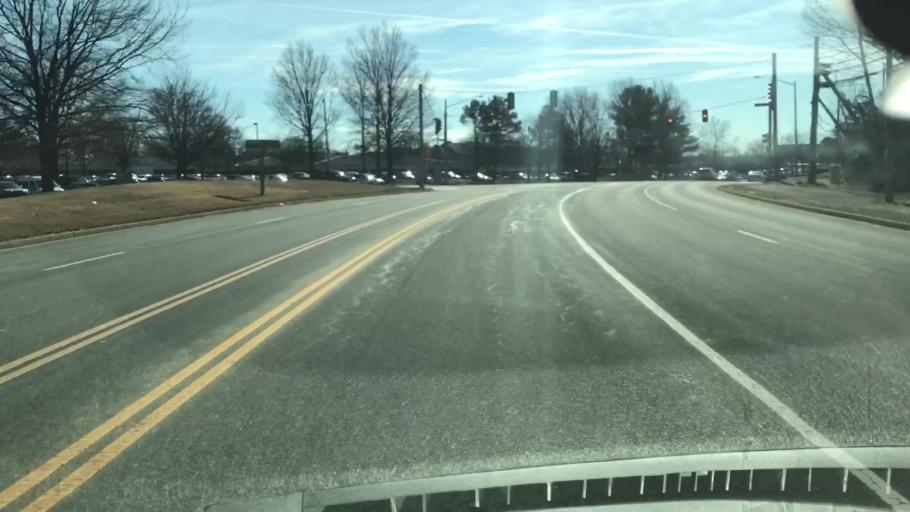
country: US
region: Virginia
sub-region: City of Fairfax
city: Fairfax
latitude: 38.8605
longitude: -77.3356
